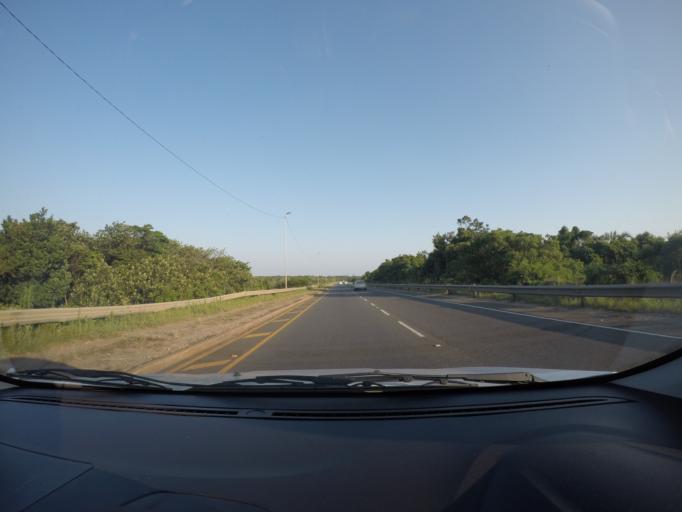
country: ZA
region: KwaZulu-Natal
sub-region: uThungulu District Municipality
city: Richards Bay
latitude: -28.7749
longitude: 32.0746
